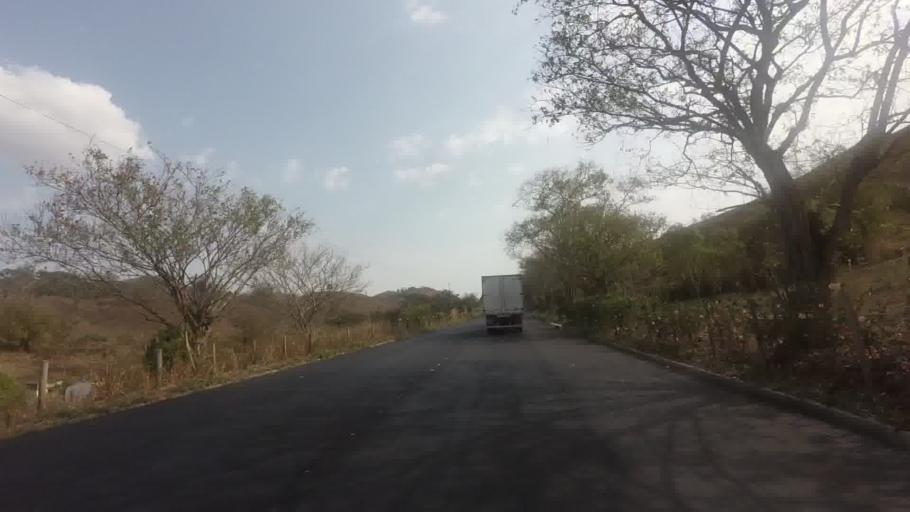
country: BR
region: Rio de Janeiro
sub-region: Bom Jesus Do Itabapoana
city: Bom Jesus do Itabapoana
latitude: -21.1609
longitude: -41.6741
